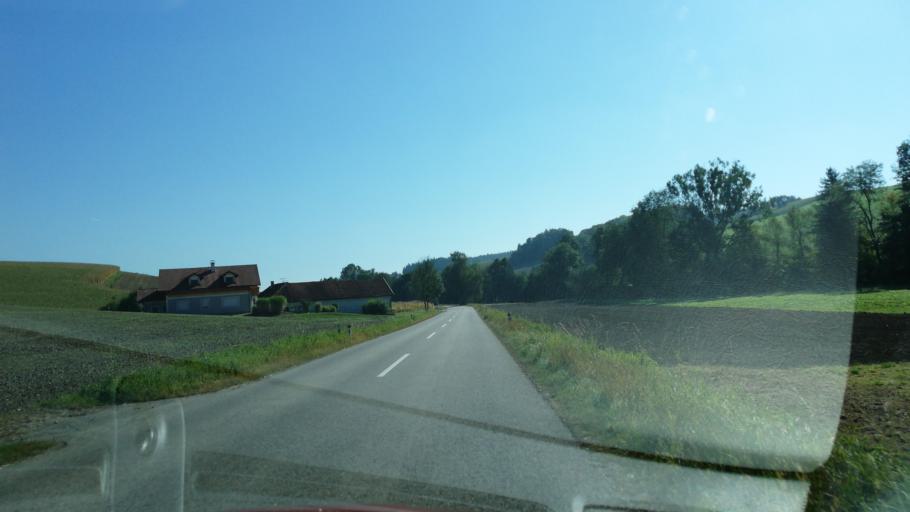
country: AT
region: Upper Austria
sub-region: Politischer Bezirk Grieskirchen
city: Grieskirchen
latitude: 48.2004
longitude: 13.8549
